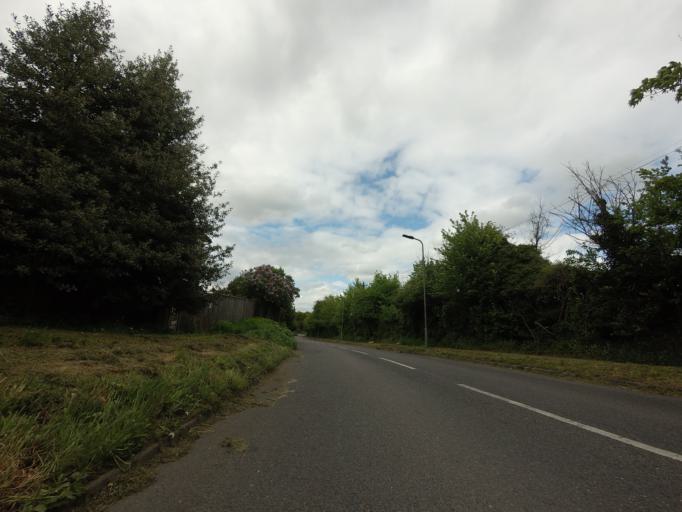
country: GB
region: England
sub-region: Greater London
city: Orpington
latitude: 51.3730
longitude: 0.1241
